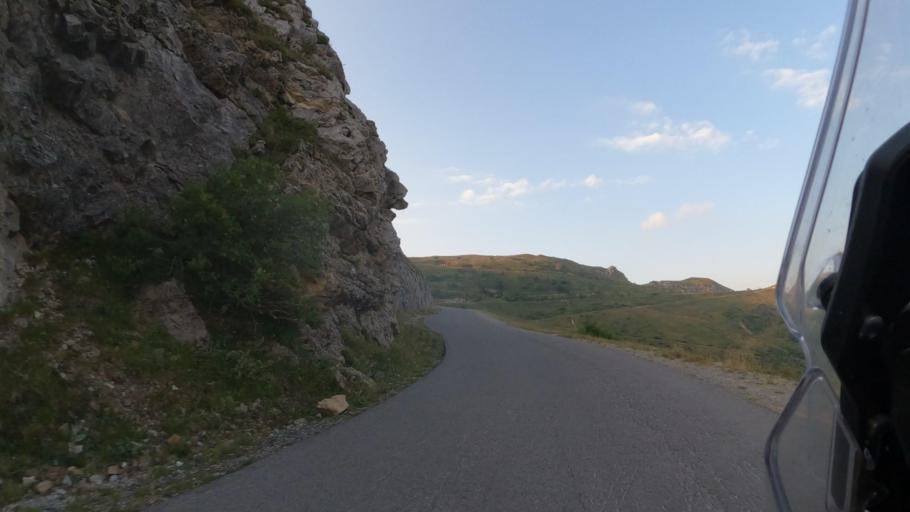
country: IT
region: Piedmont
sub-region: Provincia di Cuneo
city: Limone Piemonte
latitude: 44.1549
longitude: 7.5638
